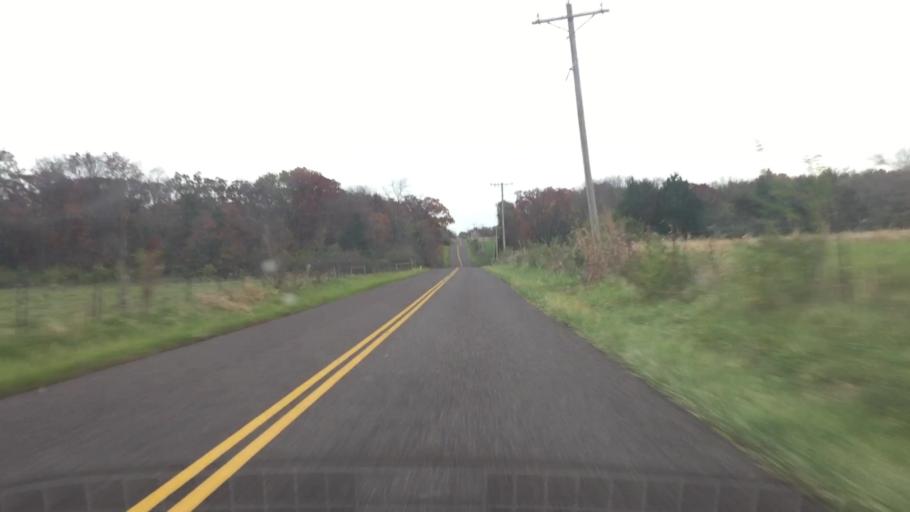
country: US
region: Missouri
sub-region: Boone County
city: Ashland
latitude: 38.8109
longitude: -92.2661
